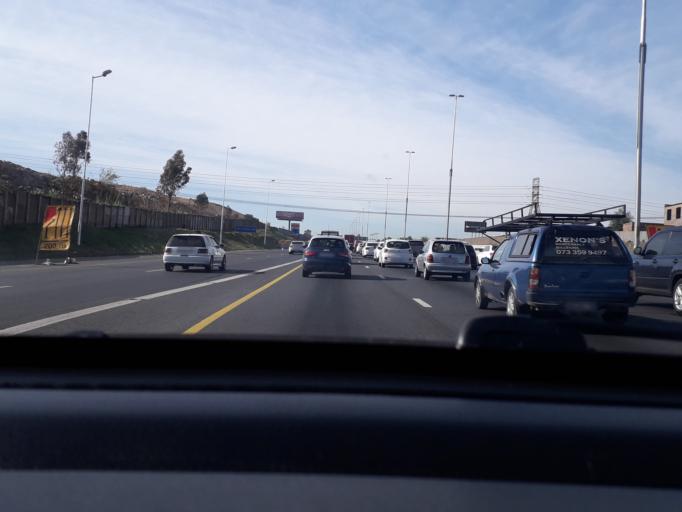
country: ZA
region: Gauteng
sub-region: City of Johannesburg Metropolitan Municipality
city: Modderfontein
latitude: -26.0854
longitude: 28.1153
